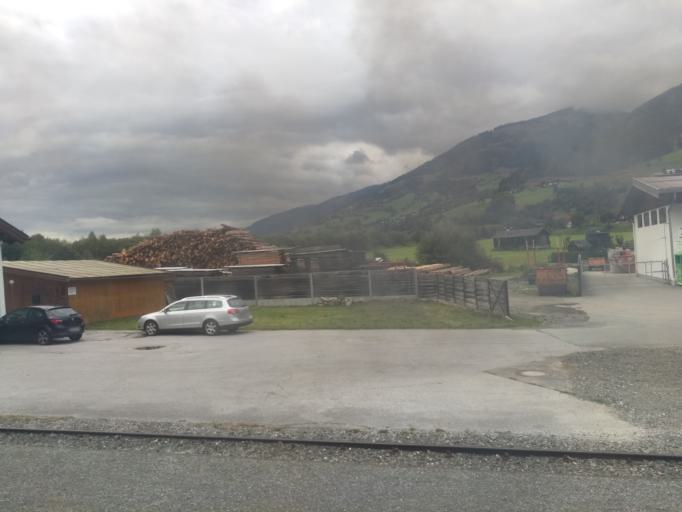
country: AT
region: Salzburg
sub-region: Politischer Bezirk Zell am See
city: Niedernsill
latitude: 47.2823
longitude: 12.6470
